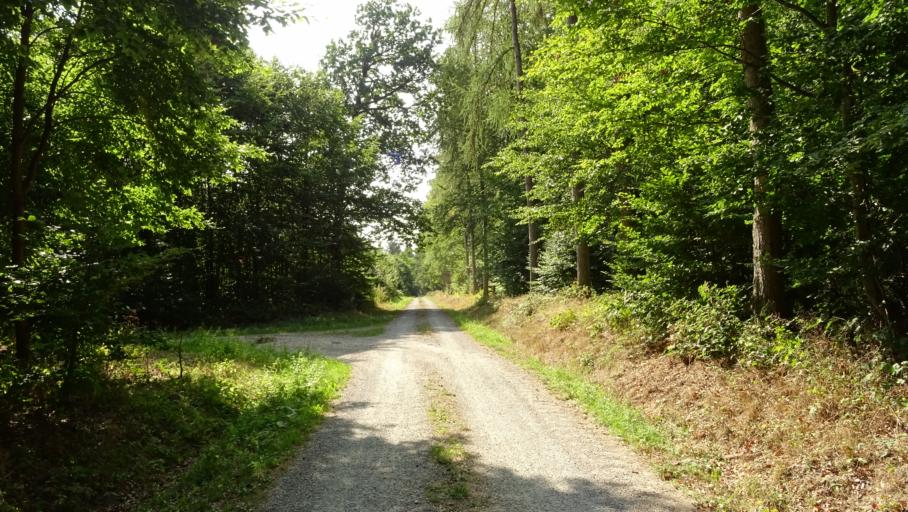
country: DE
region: Baden-Wuerttemberg
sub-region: Karlsruhe Region
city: Fahrenbach
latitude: 49.4194
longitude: 9.1373
